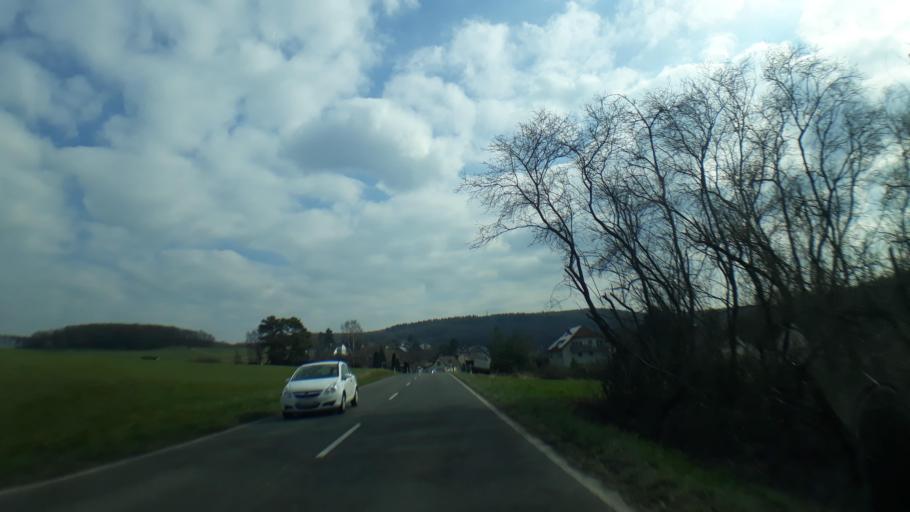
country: DE
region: North Rhine-Westphalia
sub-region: Regierungsbezirk Koln
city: Rheinbach
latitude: 50.5994
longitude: 6.8887
